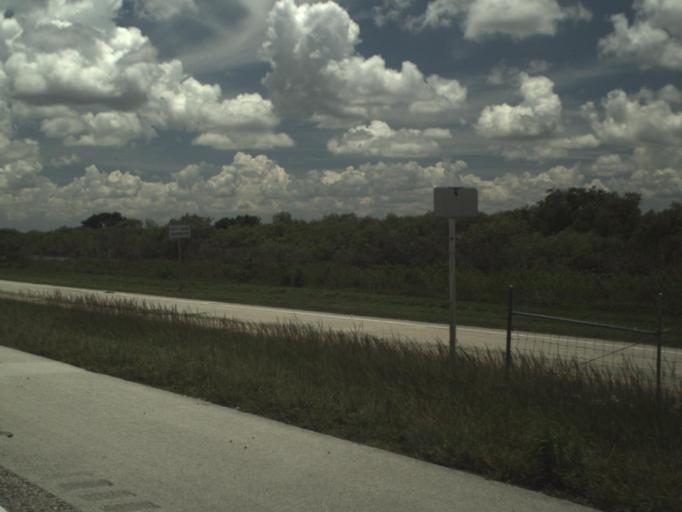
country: US
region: Florida
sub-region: Broward County
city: Weston
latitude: 26.1484
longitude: -80.7136
